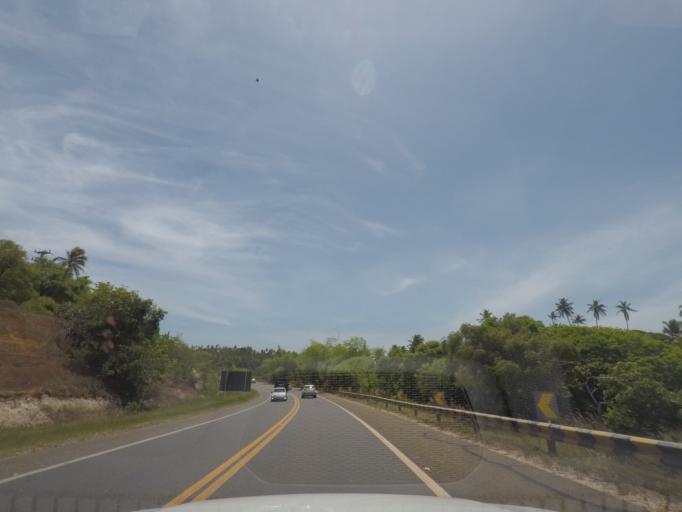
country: BR
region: Bahia
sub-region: Mata De Sao Joao
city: Mata de Sao Joao
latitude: -12.4381
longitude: -37.9507
